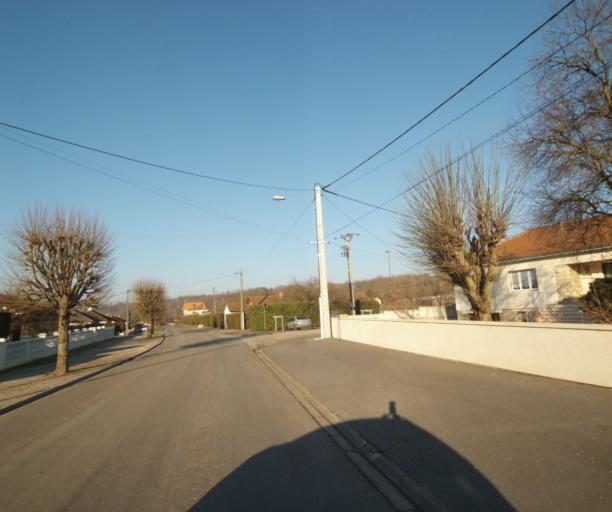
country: FR
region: Champagne-Ardenne
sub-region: Departement de la Haute-Marne
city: Bienville
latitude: 48.5774
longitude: 5.0457
